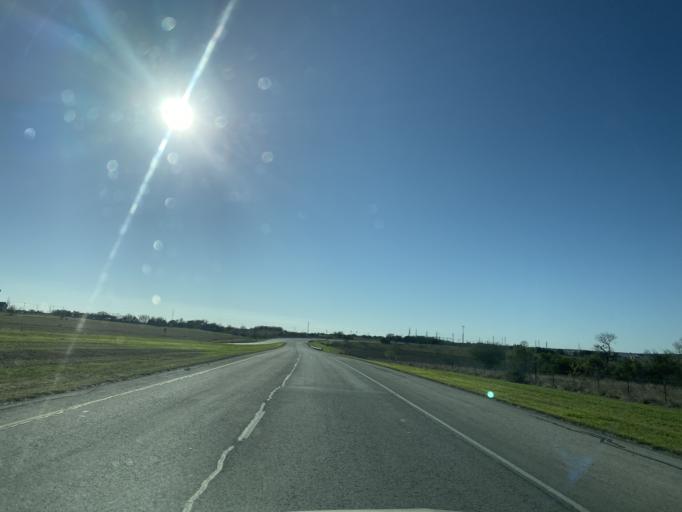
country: US
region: Texas
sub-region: Guadalupe County
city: Redwood
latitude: 29.8302
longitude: -97.9508
